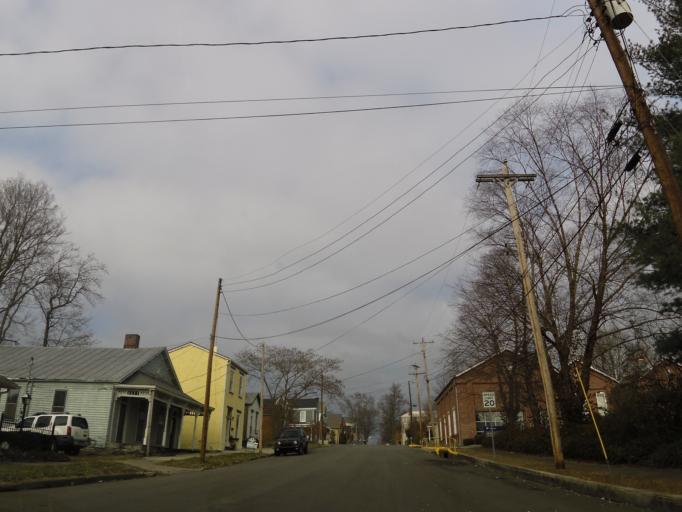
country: US
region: Indiana
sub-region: Jefferson County
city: Madison
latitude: 38.7331
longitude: -85.3757
